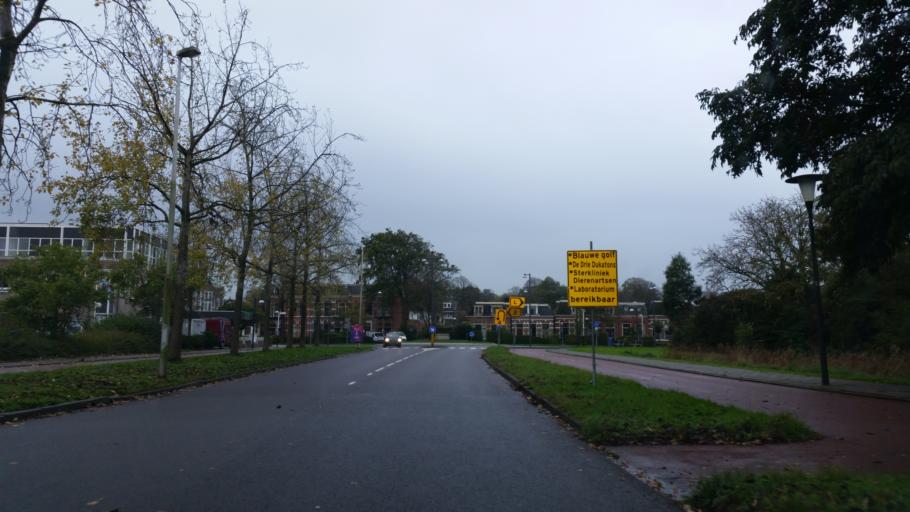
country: NL
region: Friesland
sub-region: Gemeente Leeuwarden
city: Bilgaard
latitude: 53.2079
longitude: 5.7948
